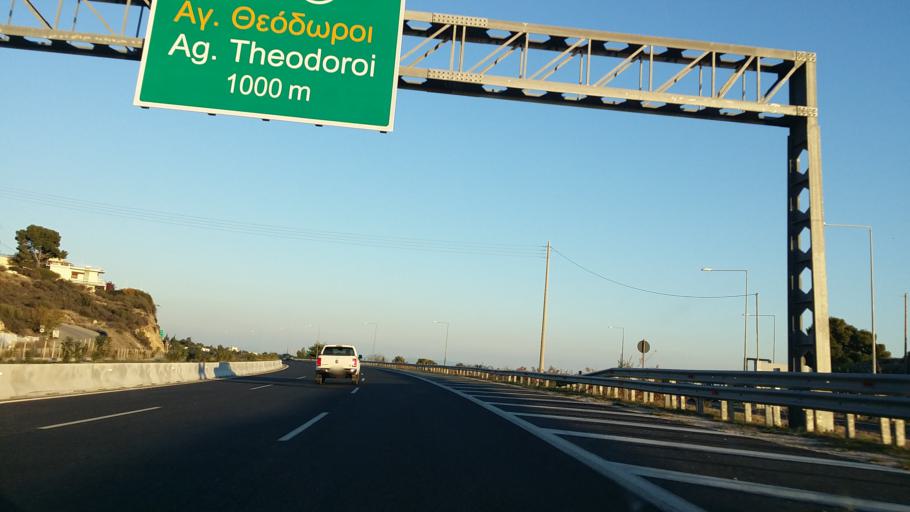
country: GR
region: Peloponnese
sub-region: Nomos Korinthias
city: Agioi Theodoroi
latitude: 37.9170
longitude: 23.1070
